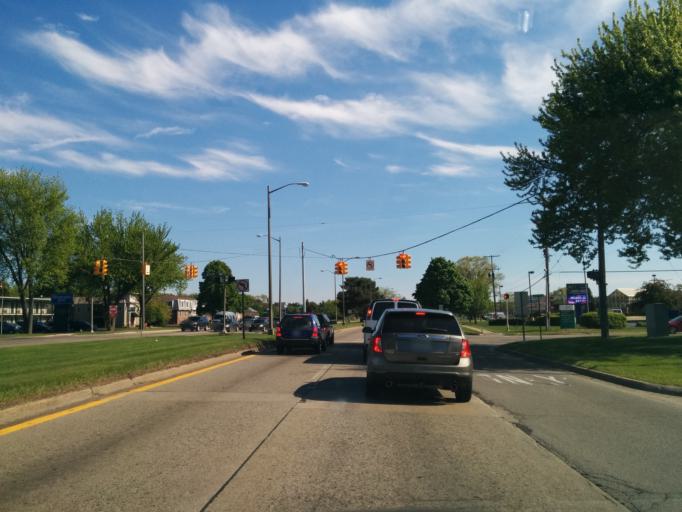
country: US
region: Michigan
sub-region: Ottawa County
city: Grand Haven
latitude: 43.0523
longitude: -86.2205
